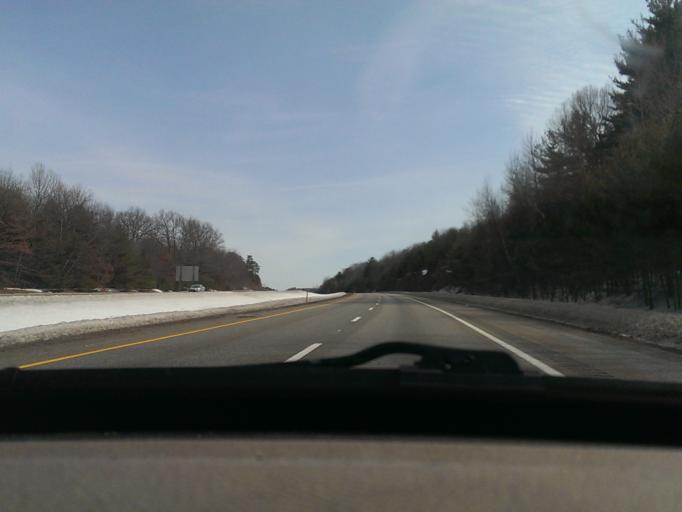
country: US
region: Massachusetts
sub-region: Worcester County
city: Millville
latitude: 42.0313
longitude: -71.6183
